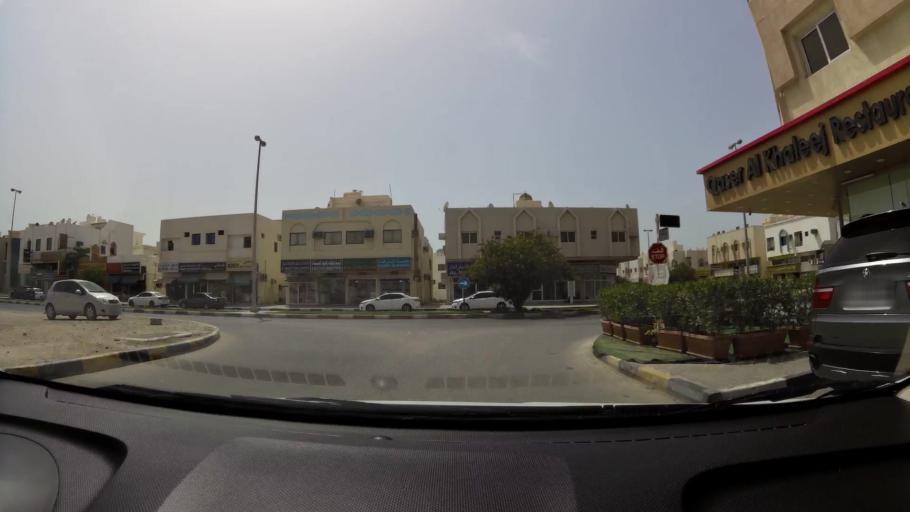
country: AE
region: Ash Shariqah
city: Sharjah
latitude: 25.3518
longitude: 55.4069
